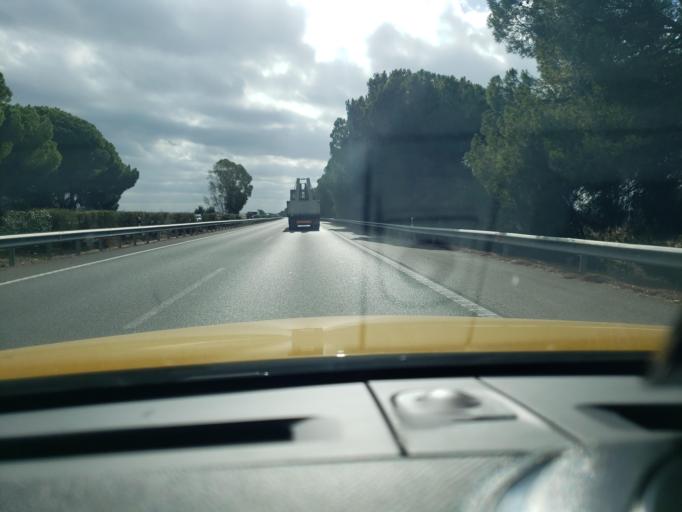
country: ES
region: Andalusia
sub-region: Provincia de Sevilla
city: Las Cabezas de San Juan
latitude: 37.0622
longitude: -5.9340
